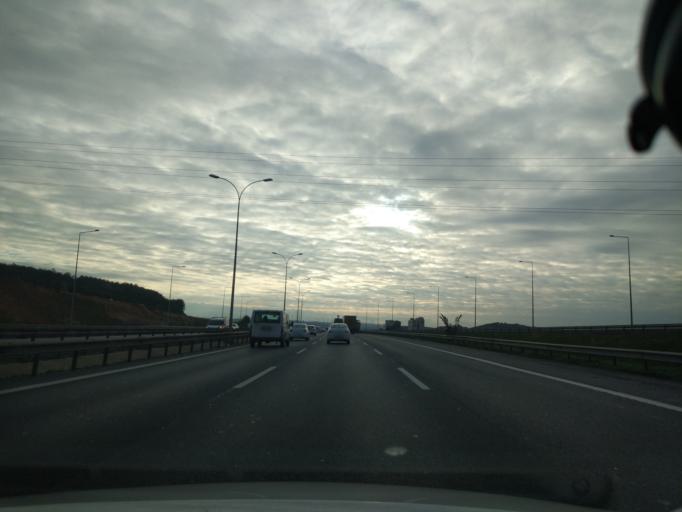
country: TR
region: Istanbul
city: Sultanbeyli
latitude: 40.9446
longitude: 29.3144
